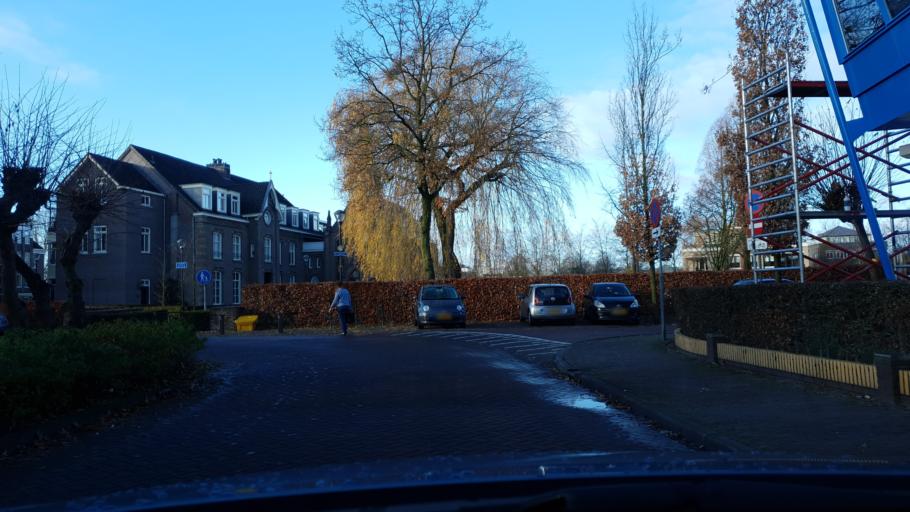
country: NL
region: Gelderland
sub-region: Gemeente Wijchen
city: Wijchen
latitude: 51.8062
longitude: 5.7242
